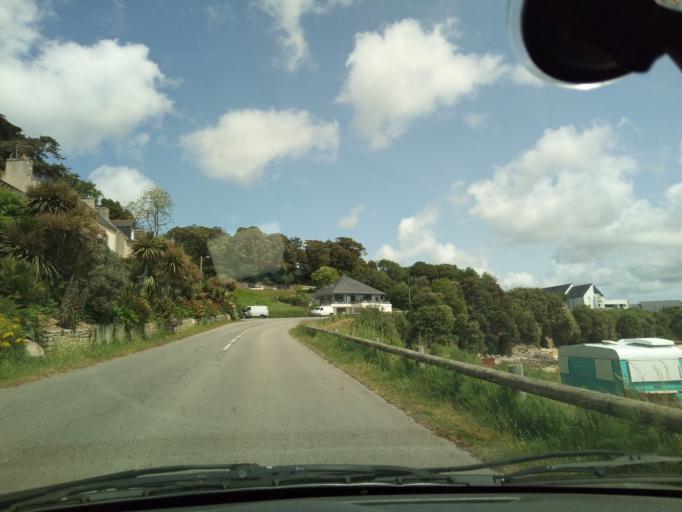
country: FR
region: Brittany
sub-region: Departement du Finistere
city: Audierne
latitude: 48.0167
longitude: -4.5384
